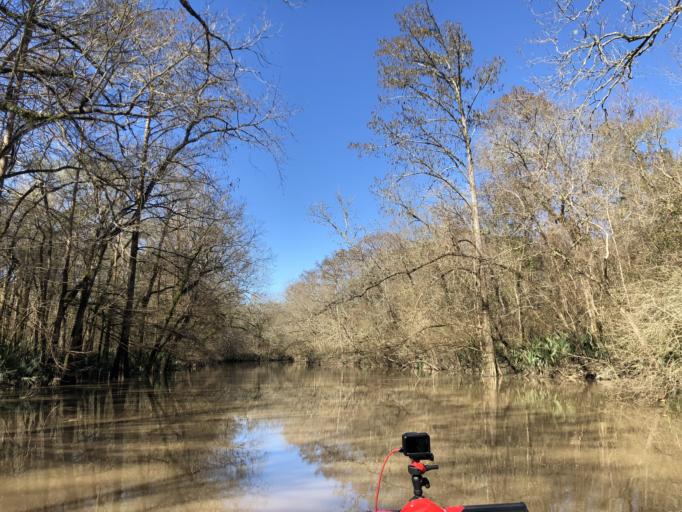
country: US
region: Louisiana
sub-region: Calcasieu Parish
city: Iowa
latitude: 30.3109
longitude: -93.0735
